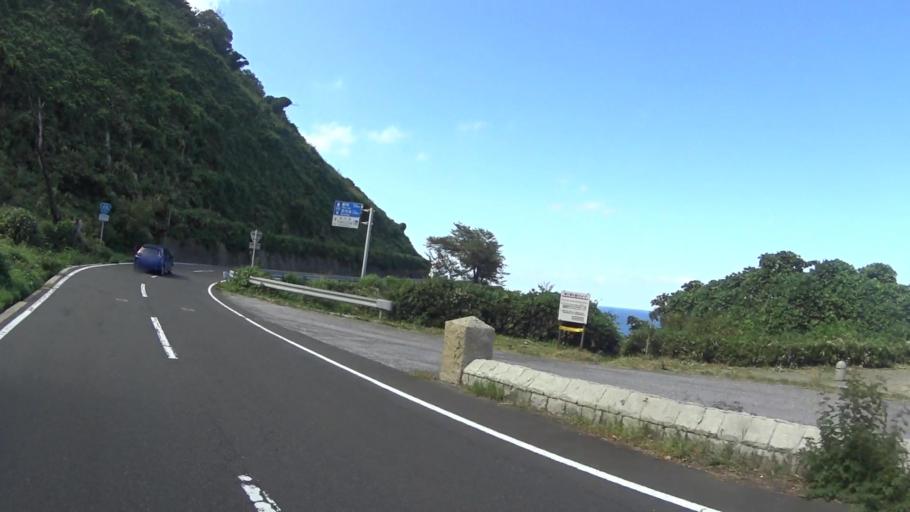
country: JP
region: Kyoto
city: Miyazu
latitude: 35.7572
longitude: 135.2454
